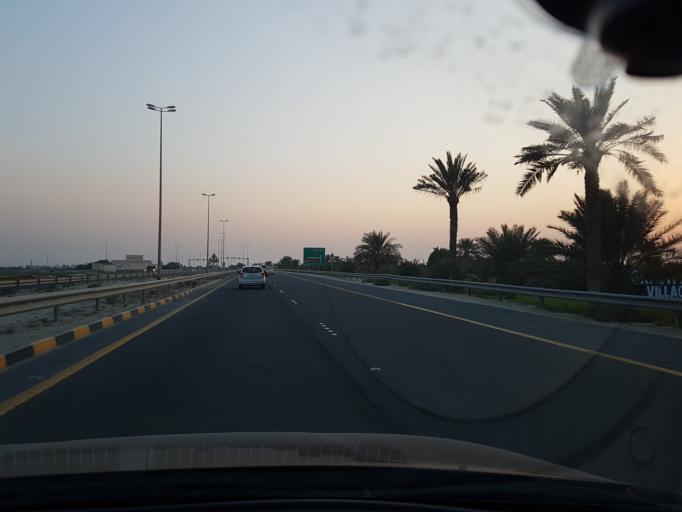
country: BH
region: Central Governorate
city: Dar Kulayb
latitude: 26.0270
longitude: 50.4957
